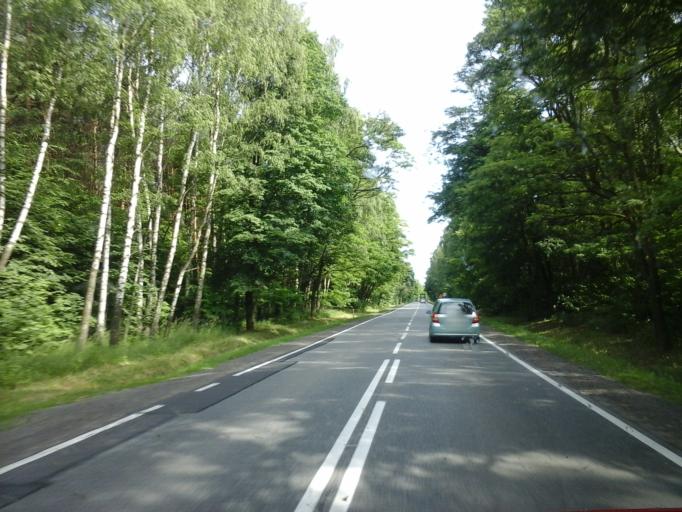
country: PL
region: Lodz Voivodeship
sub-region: Powiat opoczynski
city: Paradyz
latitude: 51.2949
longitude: 20.1253
